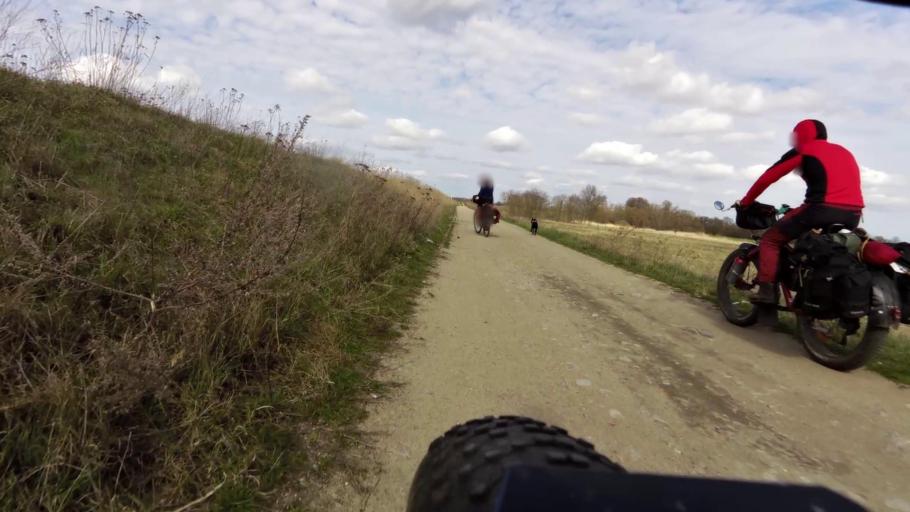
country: DE
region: Brandenburg
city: Lebus
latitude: 52.4253
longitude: 14.5478
